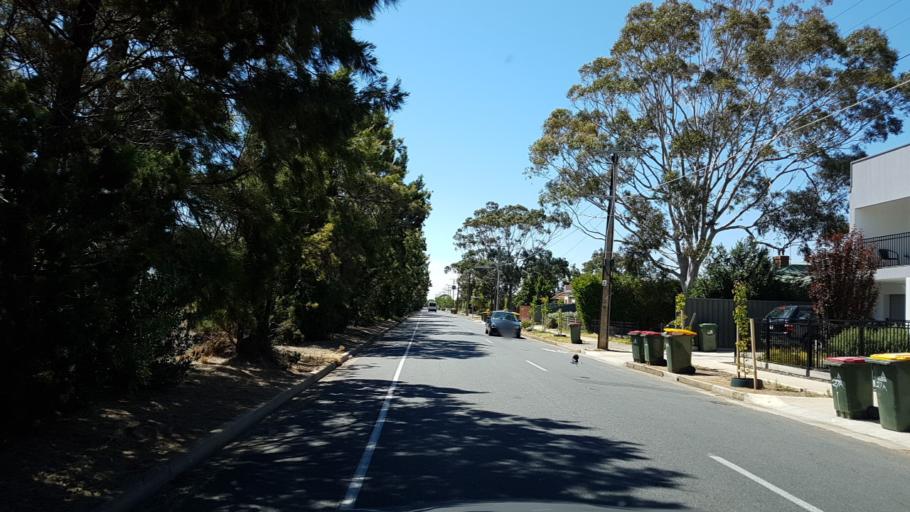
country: AU
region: South Australia
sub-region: Marion
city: Plympton Park
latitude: -34.9797
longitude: 138.5471
